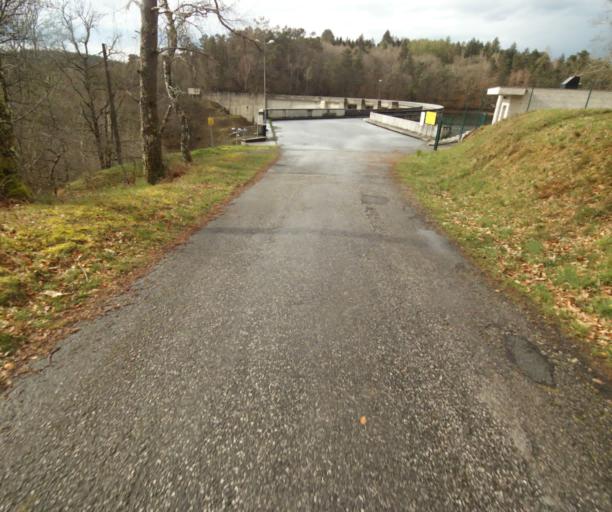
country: FR
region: Limousin
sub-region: Departement de la Correze
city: Saint-Privat
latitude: 45.2467
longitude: 1.9976
